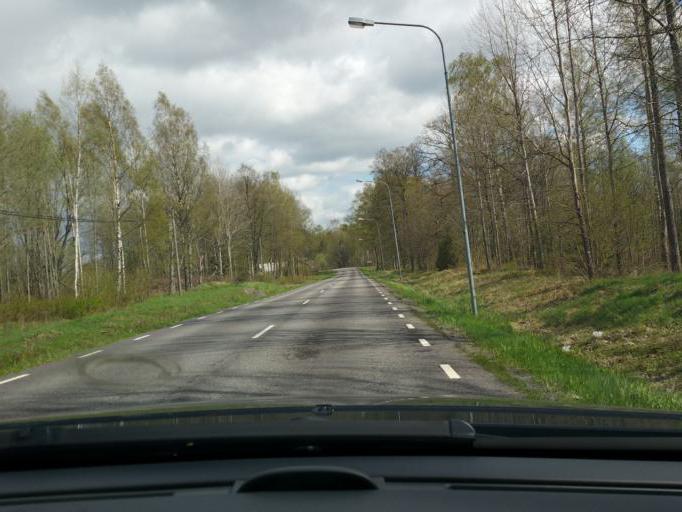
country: SE
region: Kronoberg
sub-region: Vaxjo Kommun
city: Lammhult
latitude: 57.1757
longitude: 14.6029
